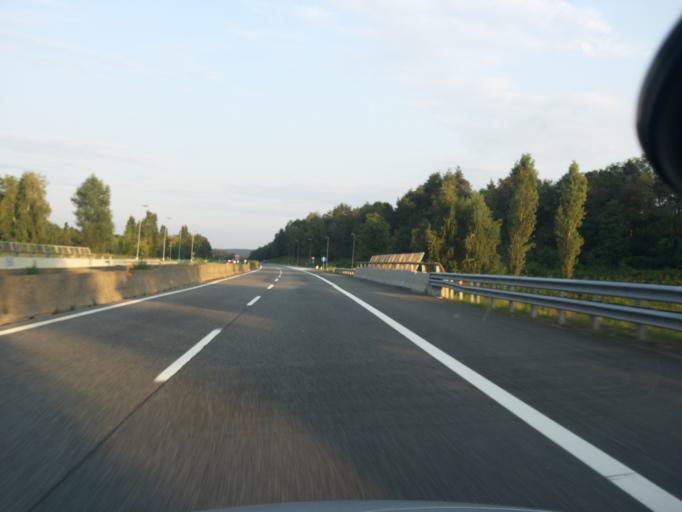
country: IT
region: Piedmont
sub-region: Provincia di Novara
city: Paruzzaro
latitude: 45.7317
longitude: 8.5102
